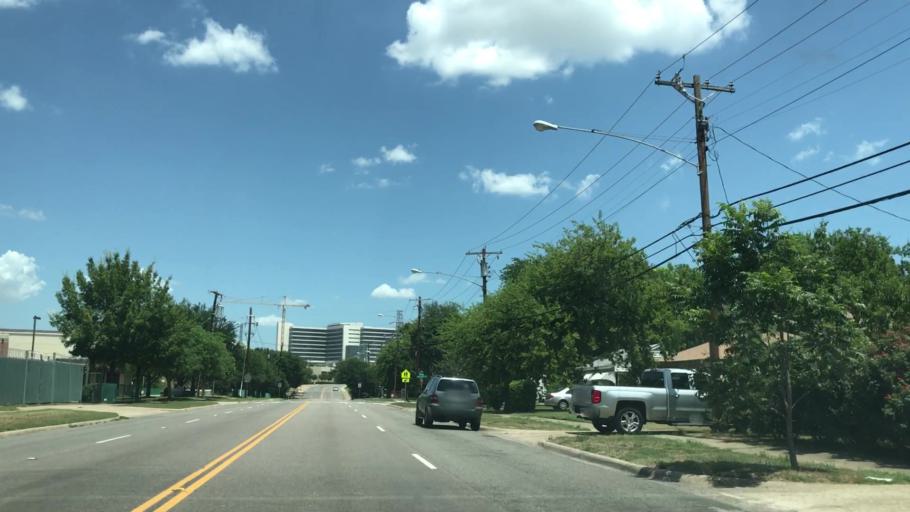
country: US
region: Texas
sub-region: Dallas County
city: Dallas
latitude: 32.8163
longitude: -96.8593
